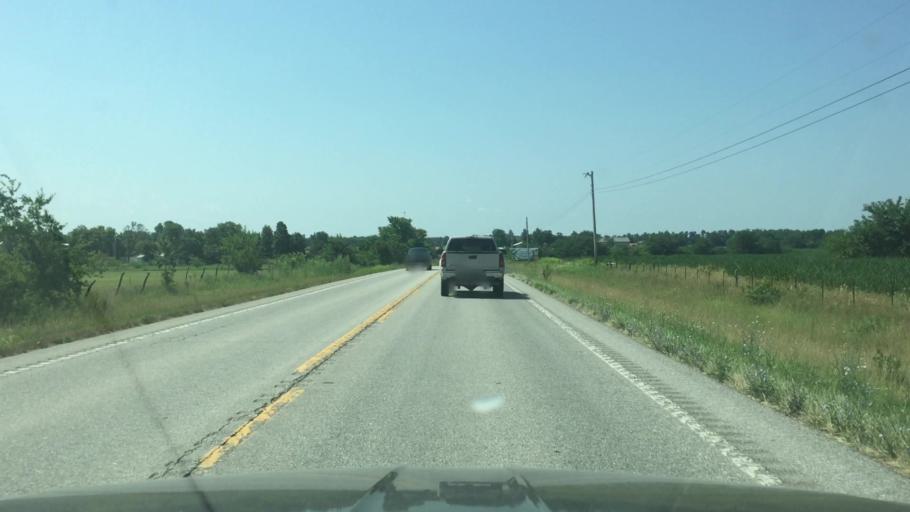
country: US
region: Missouri
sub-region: Morgan County
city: Versailles
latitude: 38.4565
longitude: -92.8091
